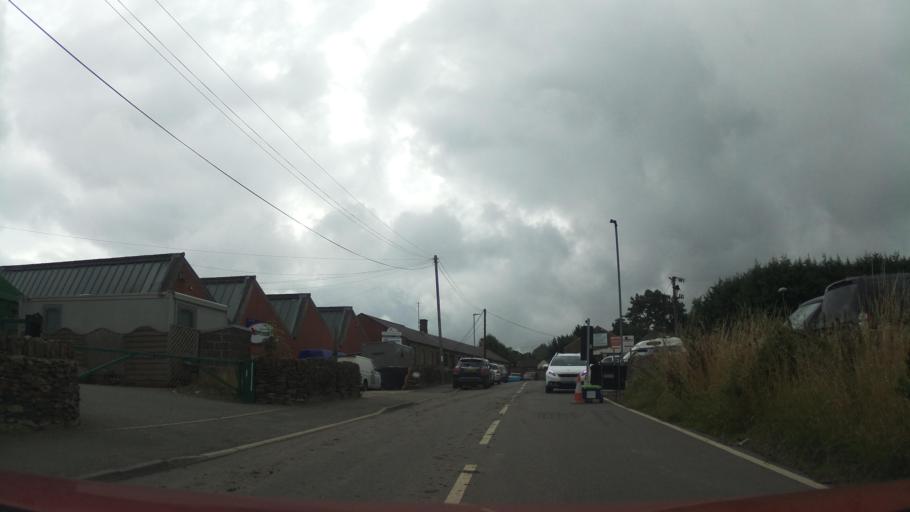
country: GB
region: England
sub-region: Kirklees
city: Shelley
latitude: 53.5917
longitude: -1.6882
